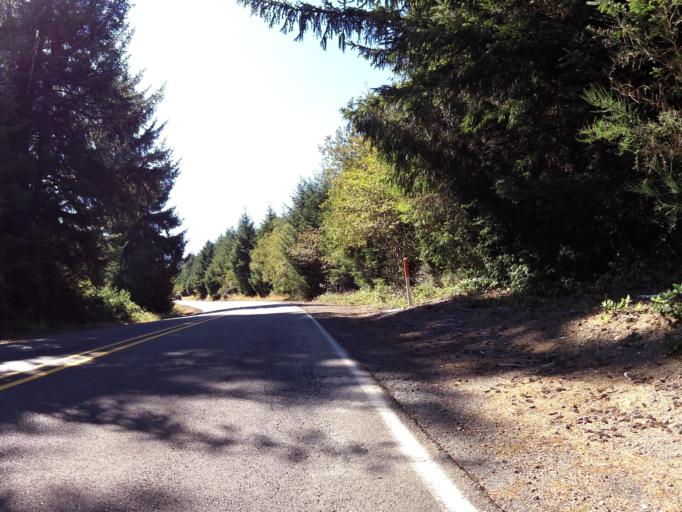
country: US
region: Oregon
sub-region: Coos County
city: Barview
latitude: 43.2803
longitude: -124.3456
